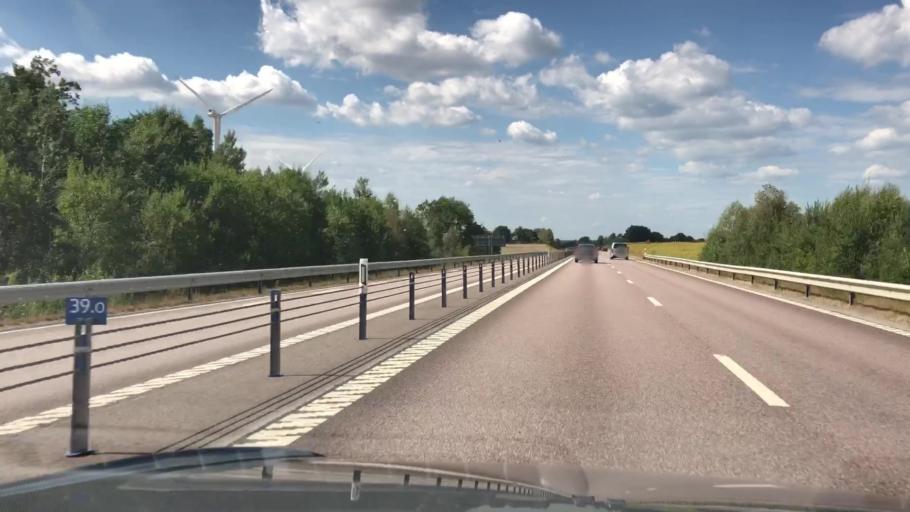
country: SE
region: Kalmar
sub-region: Kalmar Kommun
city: Ljungbyholm
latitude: 56.6206
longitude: 16.1617
